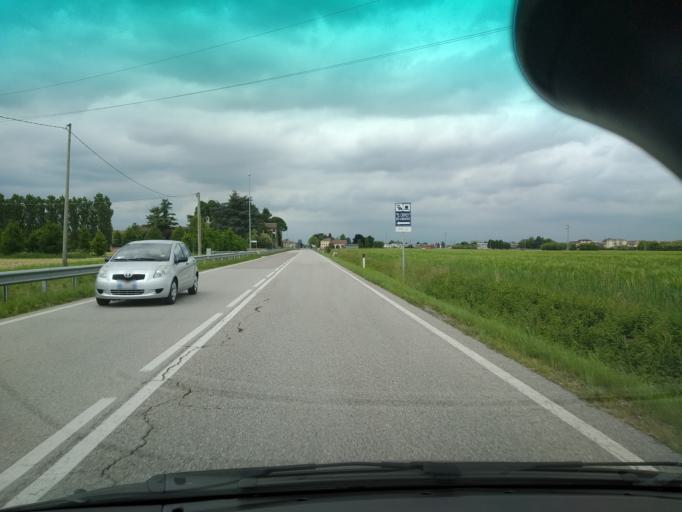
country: IT
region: Veneto
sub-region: Provincia di Padova
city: Tremignon
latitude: 45.5131
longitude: 11.8101
